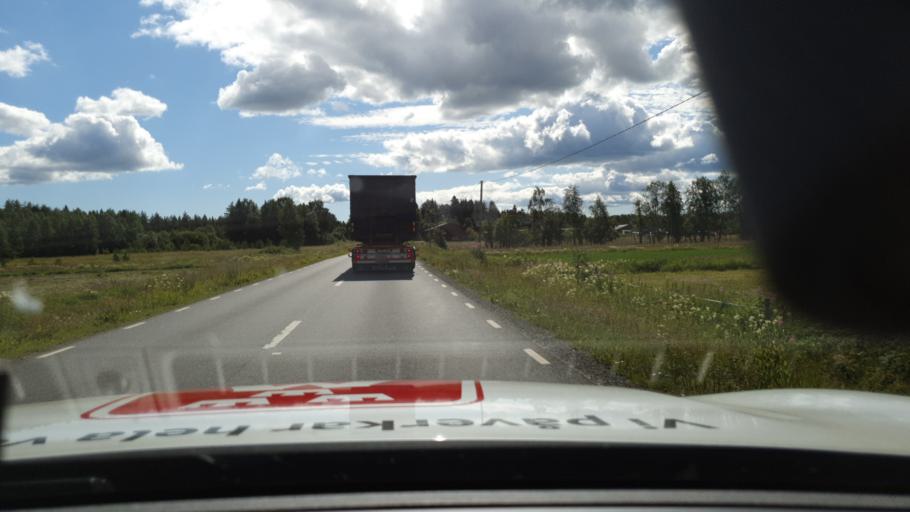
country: SE
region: Norrbotten
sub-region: Lulea Kommun
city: Gammelstad
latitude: 65.7945
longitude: 22.0718
